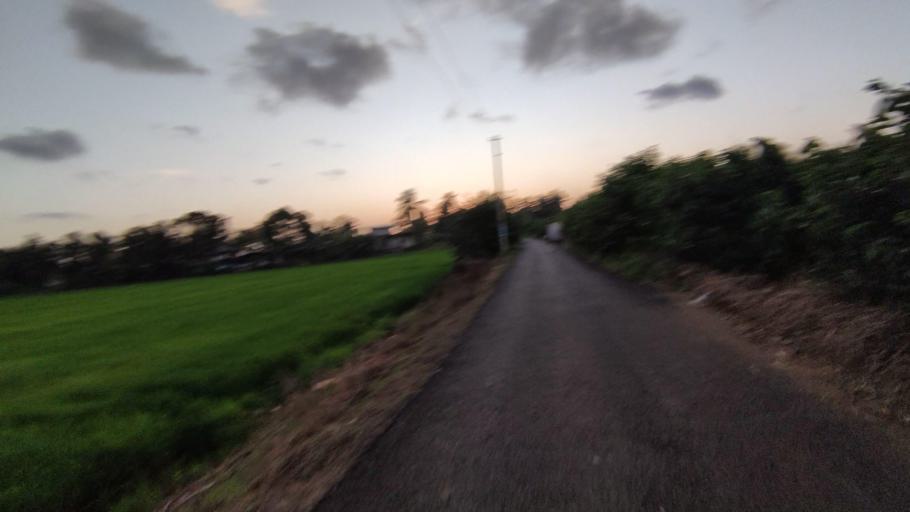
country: IN
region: Kerala
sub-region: Kottayam
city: Kottayam
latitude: 9.5887
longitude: 76.4496
